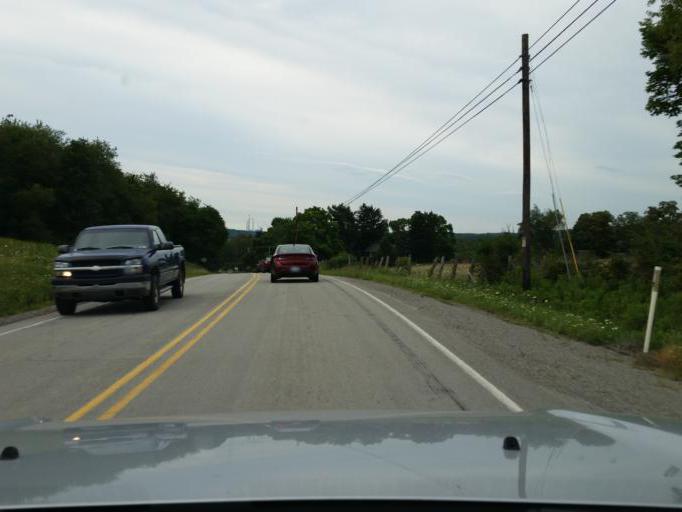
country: US
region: Pennsylvania
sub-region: Indiana County
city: Blairsville
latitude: 40.3912
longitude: -79.2624
